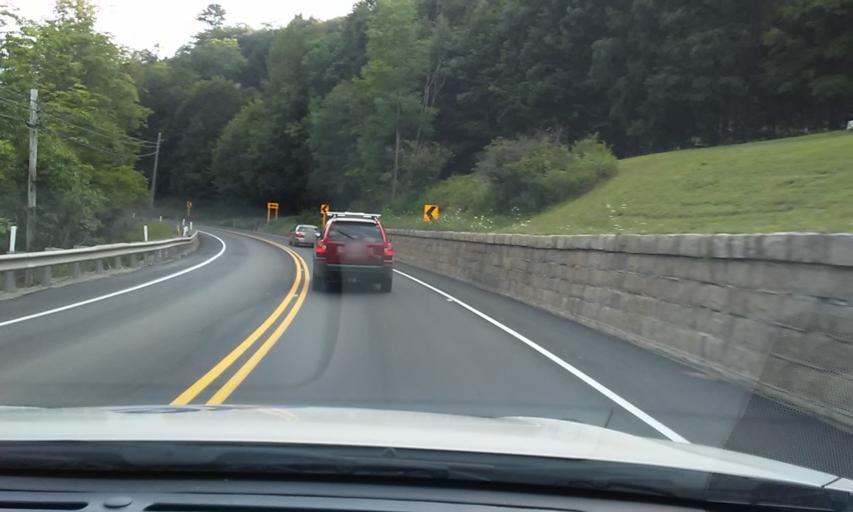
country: US
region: Pennsylvania
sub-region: Potter County
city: Coudersport
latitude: 41.7574
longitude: -78.0538
